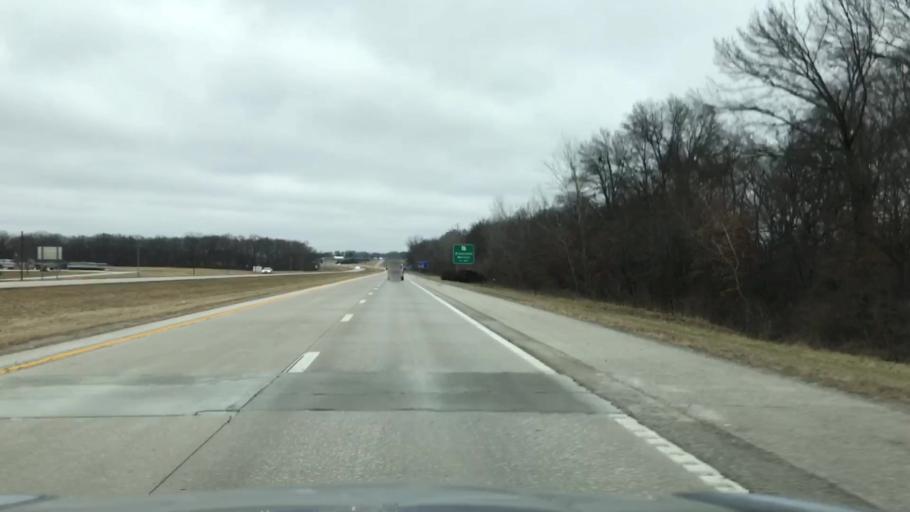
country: US
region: Missouri
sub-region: Linn County
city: Brookfield
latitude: 39.7756
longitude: -93.0898
